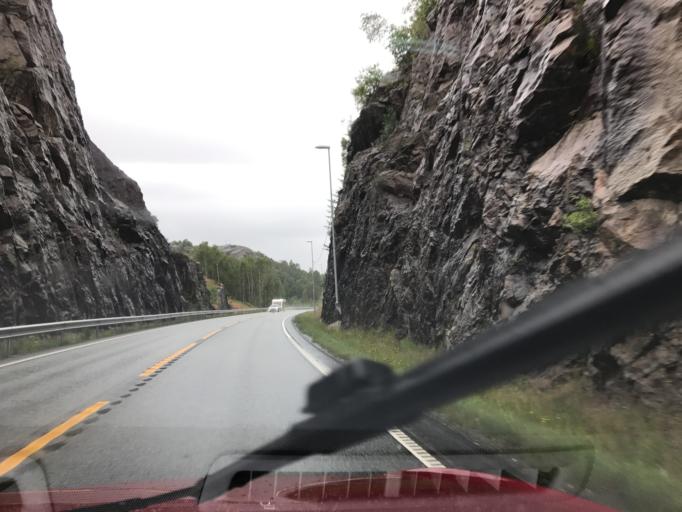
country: NO
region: Rogaland
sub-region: Bjerkreim
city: Vikesa
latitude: 58.5447
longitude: 6.0631
